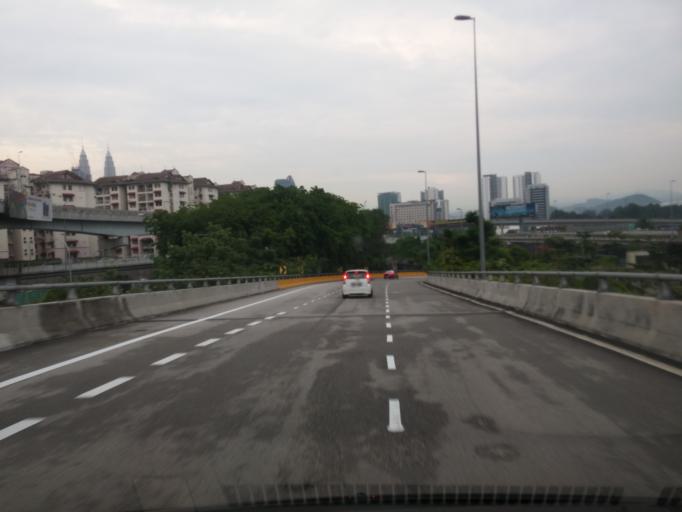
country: MY
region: Kuala Lumpur
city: Kuala Lumpur
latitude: 3.1355
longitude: 101.7193
